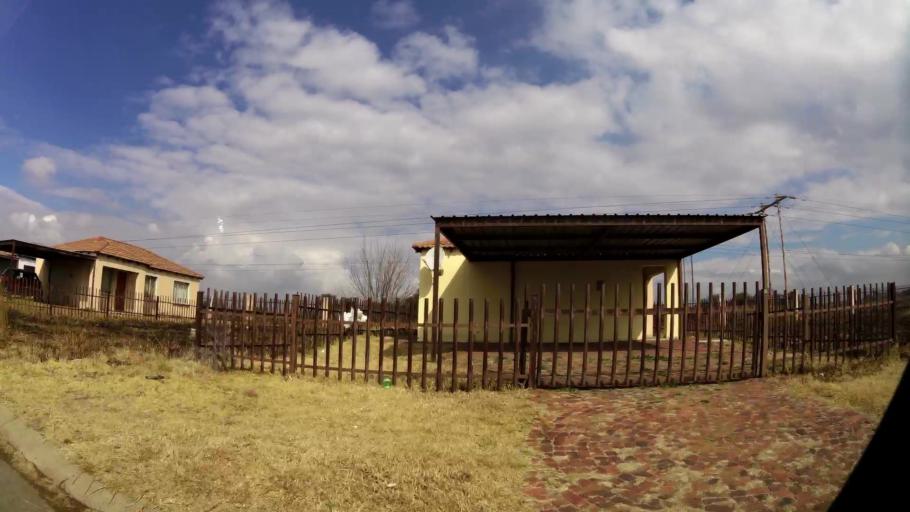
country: ZA
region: Gauteng
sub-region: Sedibeng District Municipality
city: Vanderbijlpark
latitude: -26.7166
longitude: 27.8819
